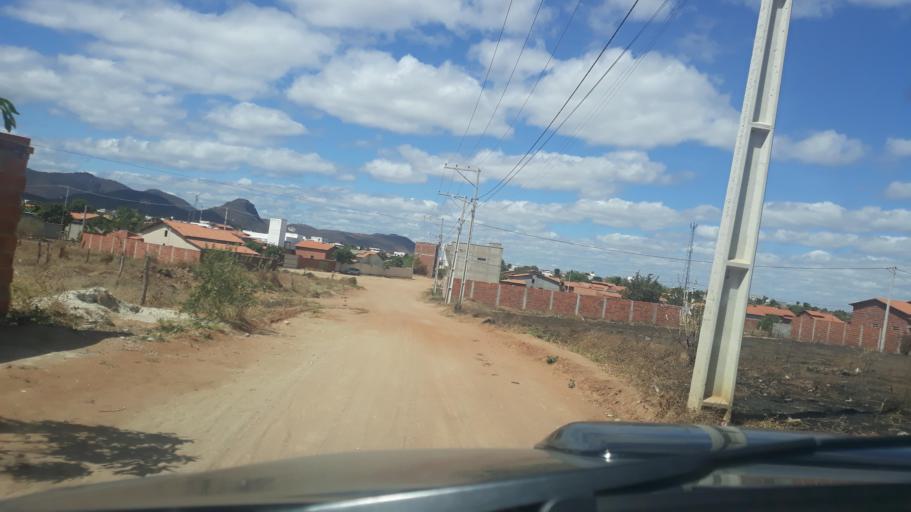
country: BR
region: Bahia
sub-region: Riacho De Santana
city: Riacho de Santana
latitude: -13.9052
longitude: -42.8502
